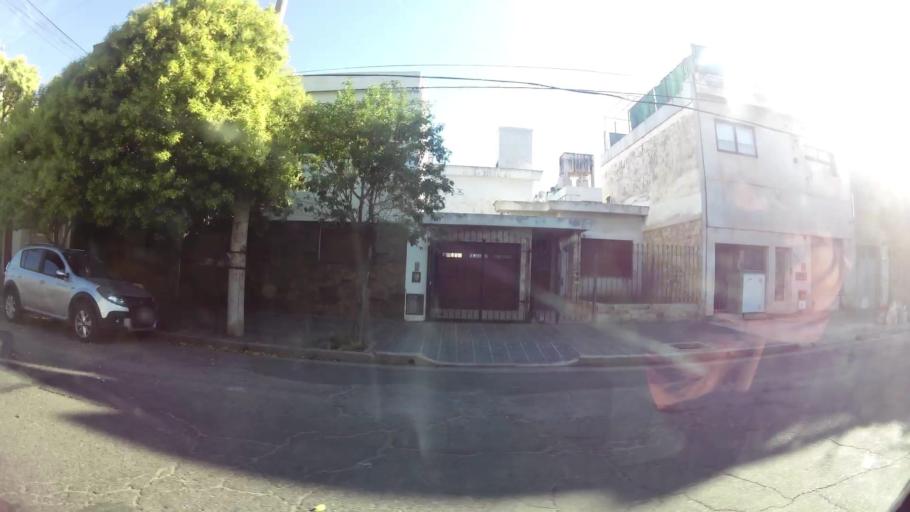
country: AR
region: Cordoba
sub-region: Departamento de Capital
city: Cordoba
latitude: -31.3952
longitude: -64.1796
